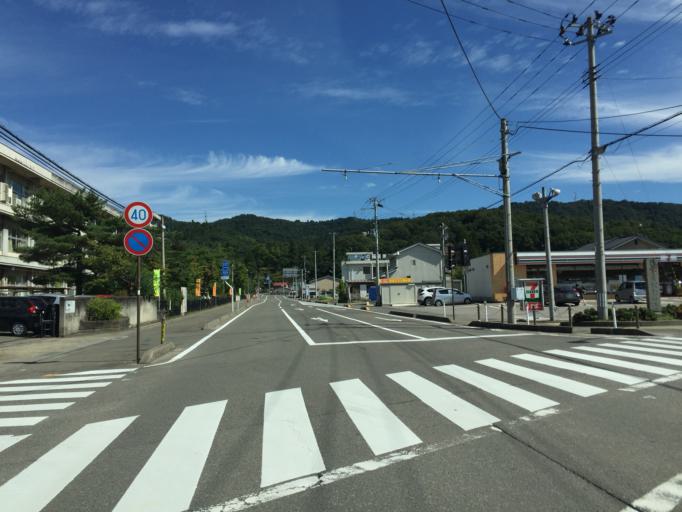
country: JP
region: Fukushima
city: Fukushima-shi
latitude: 37.7712
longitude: 140.5094
